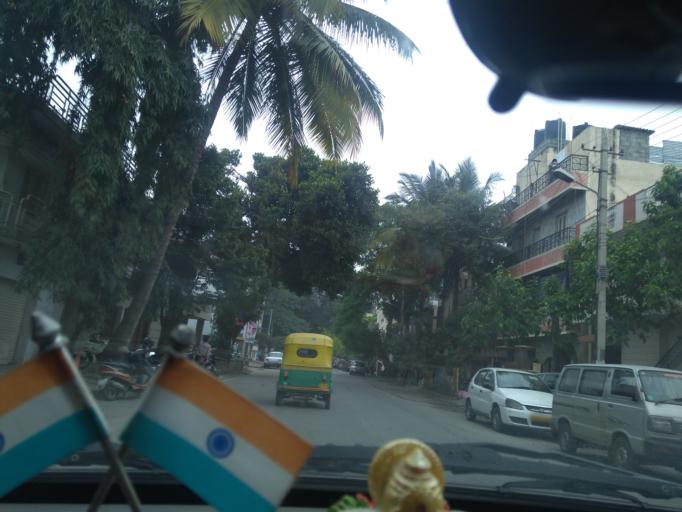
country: IN
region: Karnataka
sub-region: Bangalore Urban
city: Bangalore
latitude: 12.9879
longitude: 77.5524
